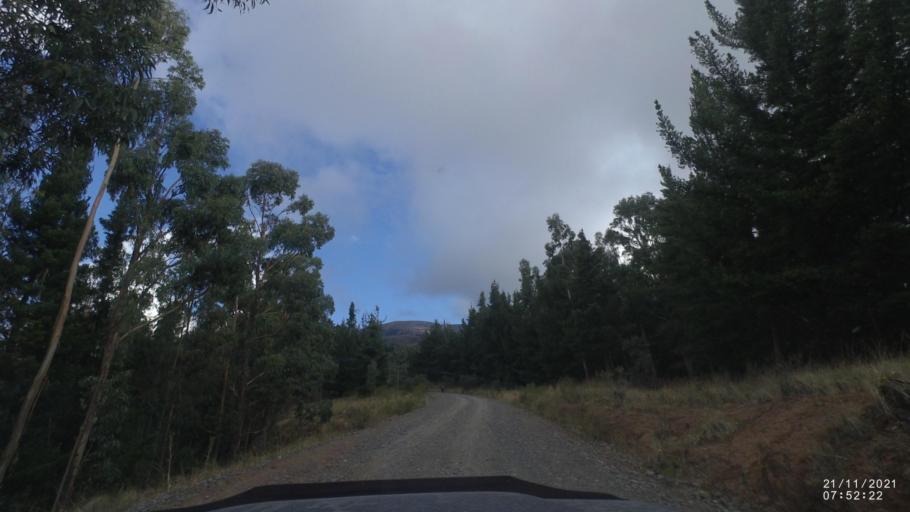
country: BO
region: Cochabamba
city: Cochabamba
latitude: -17.3060
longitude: -66.2182
